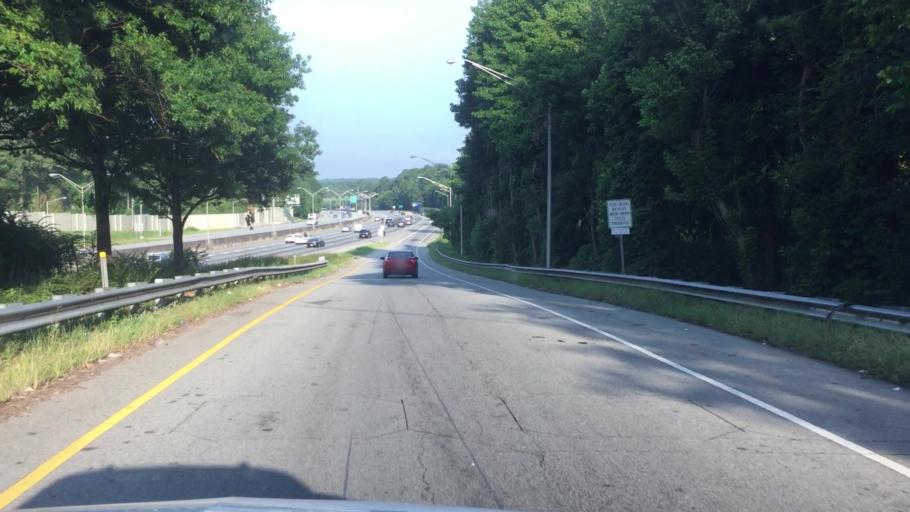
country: US
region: Georgia
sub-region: DeKalb County
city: Panthersville
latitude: 33.7167
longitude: -84.2529
